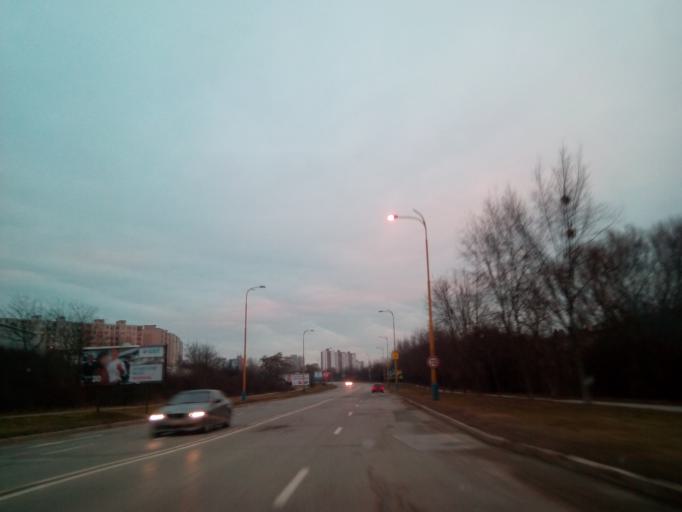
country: SK
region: Kosicky
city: Kosice
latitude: 48.7060
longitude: 21.2194
